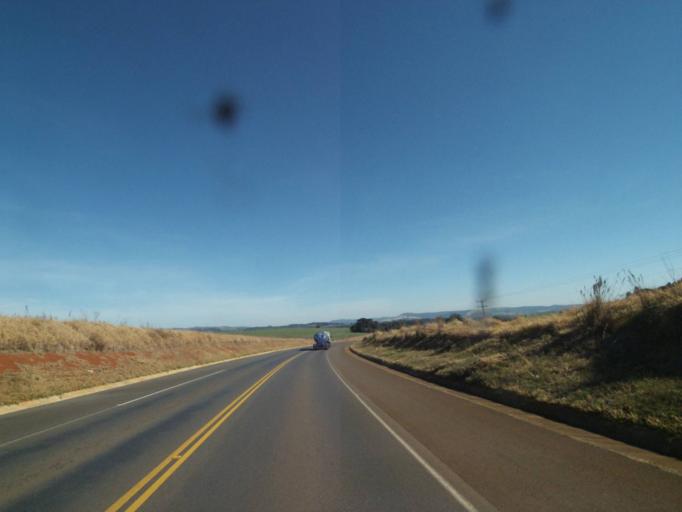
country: BR
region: Parana
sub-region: Tibagi
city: Tibagi
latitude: -24.4593
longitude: -50.4256
